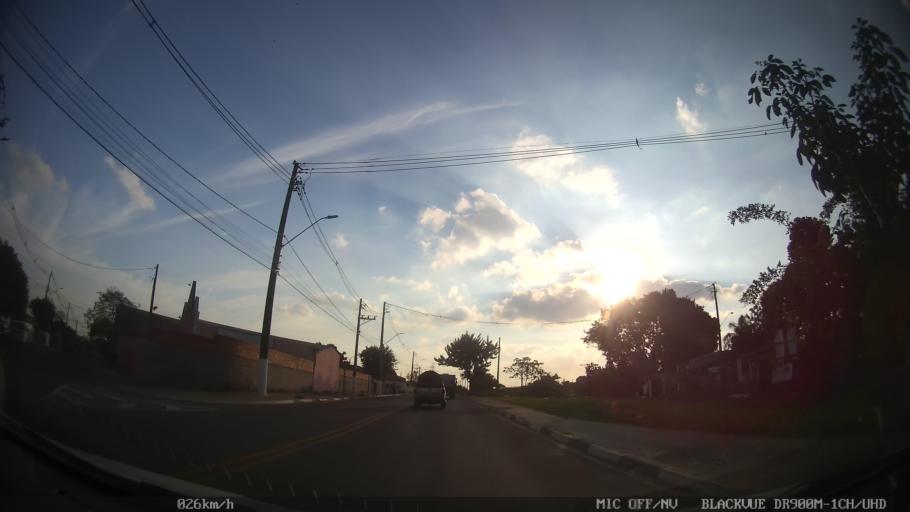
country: BR
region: Sao Paulo
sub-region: Hortolandia
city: Hortolandia
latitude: -22.8590
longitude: -47.1617
